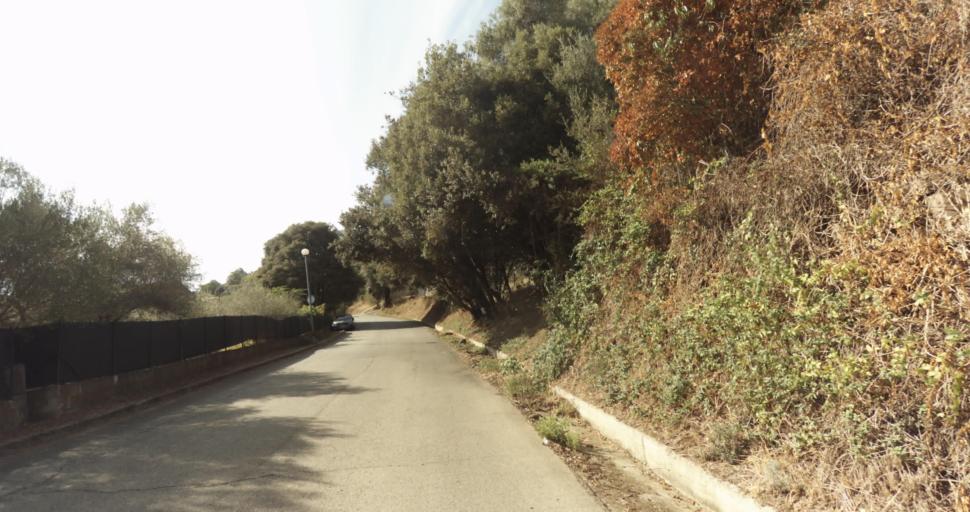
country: FR
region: Corsica
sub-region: Departement de la Corse-du-Sud
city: Ajaccio
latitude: 41.9337
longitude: 8.7226
